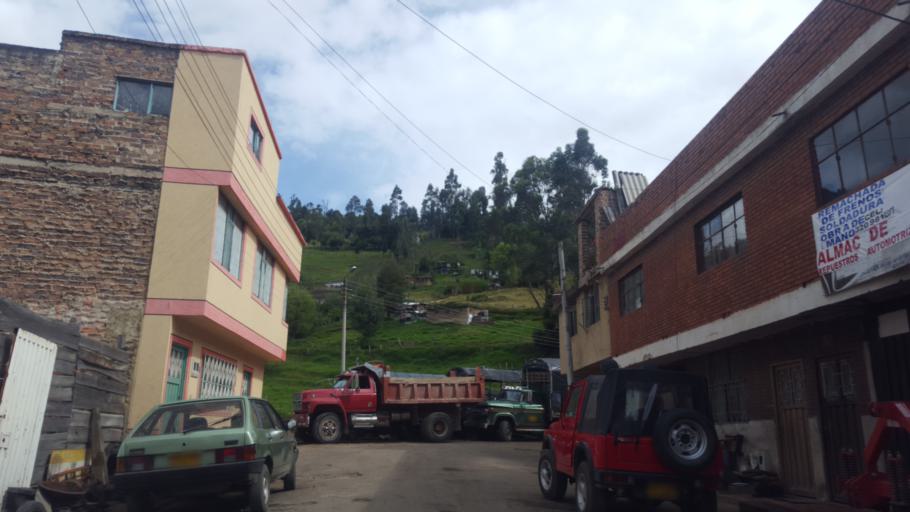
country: CO
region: Boyaca
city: Belen
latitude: 5.9870
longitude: -72.9164
